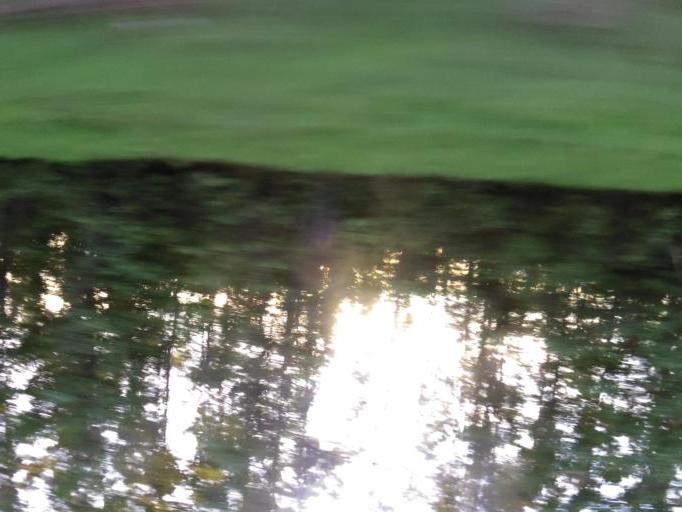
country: US
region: Georgia
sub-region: Camden County
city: Woodbine
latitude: 31.0135
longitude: -81.7316
